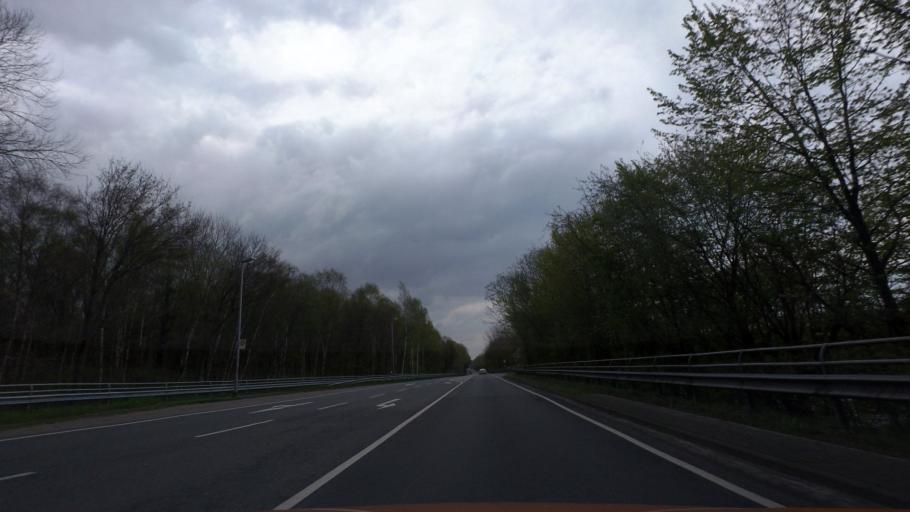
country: DE
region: Lower Saxony
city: Wardenburg
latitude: 53.1081
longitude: 8.1306
